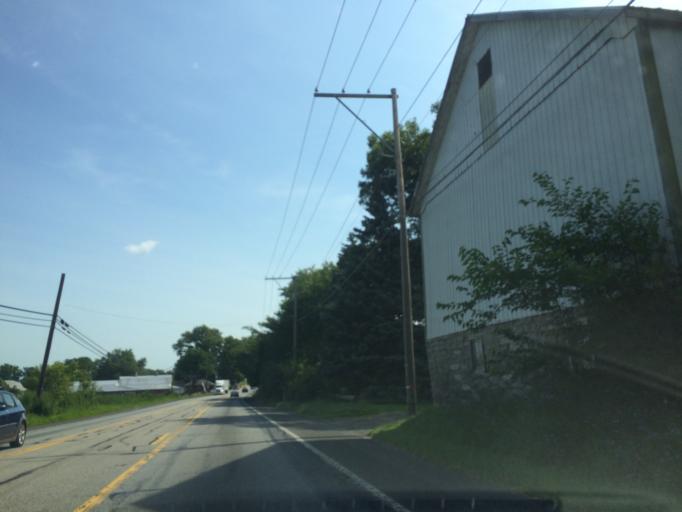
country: US
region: Pennsylvania
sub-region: Berks County
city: Fleetwood
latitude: 40.4804
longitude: -75.8504
